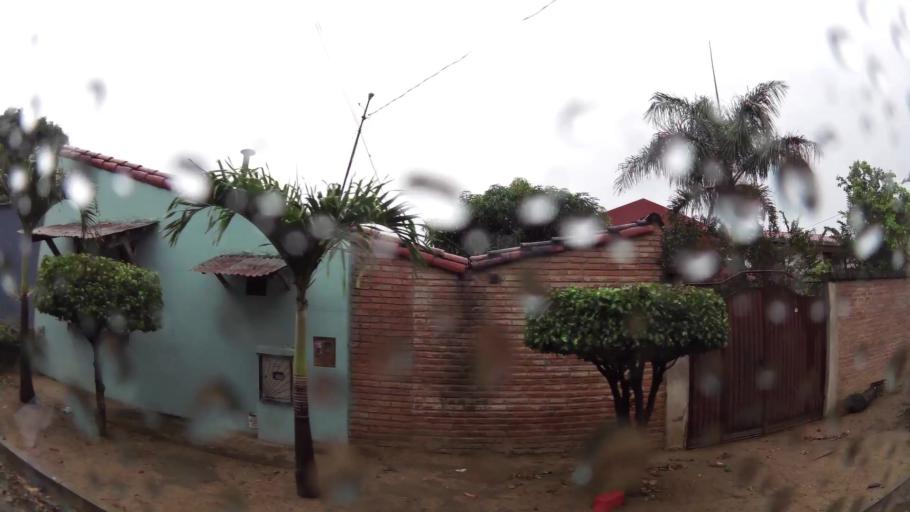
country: BO
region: Santa Cruz
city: Santa Cruz de la Sierra
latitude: -17.8151
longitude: -63.2265
